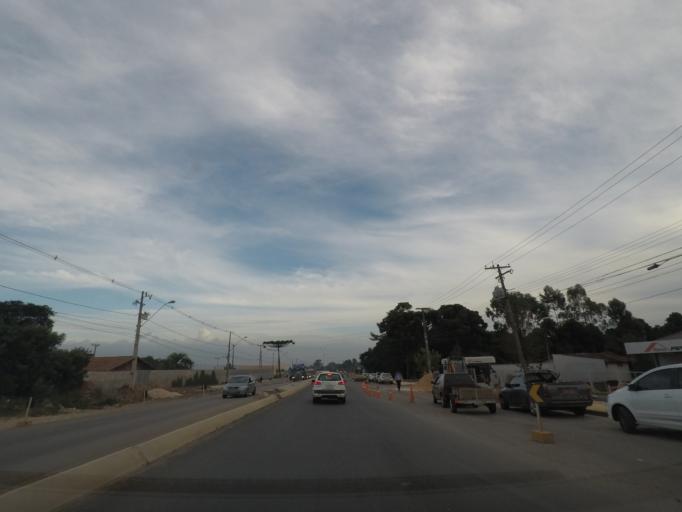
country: BR
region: Parana
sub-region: Colombo
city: Colombo
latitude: -25.3299
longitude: -49.2210
